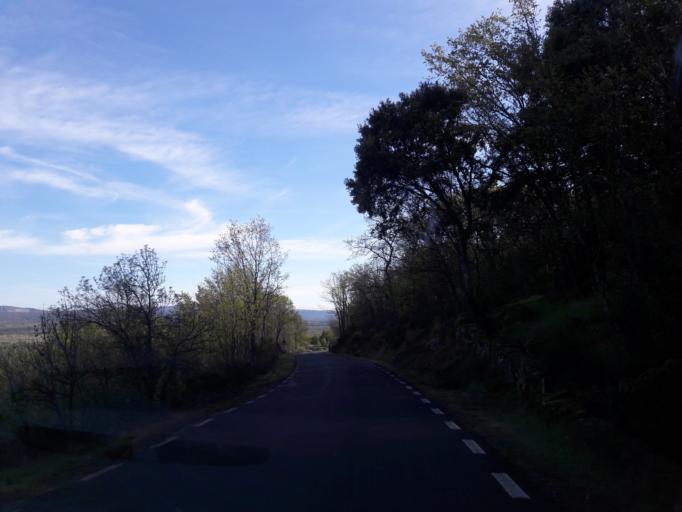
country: ES
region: Castille and Leon
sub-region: Provincia de Salamanca
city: Navalmoral de Bejar
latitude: 40.4290
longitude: -5.7802
